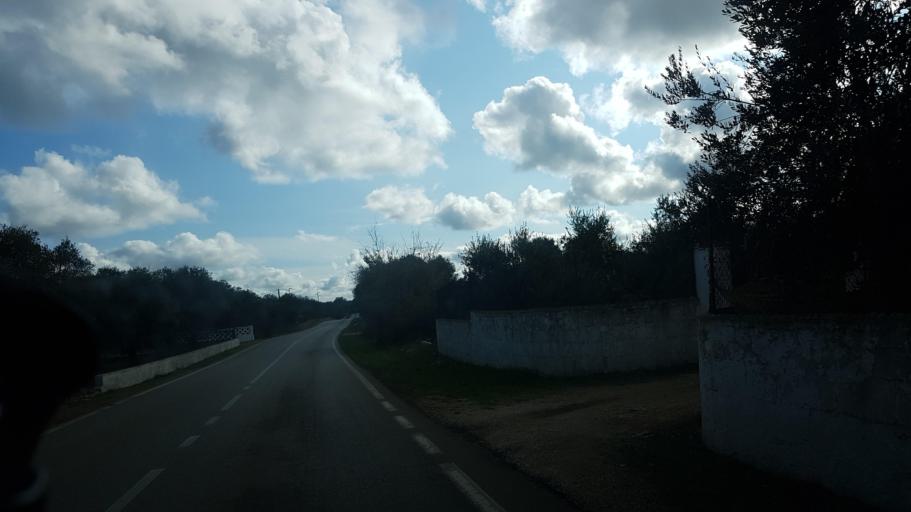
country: IT
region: Apulia
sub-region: Provincia di Brindisi
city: San Michele Salentino
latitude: 40.6614
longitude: 17.6004
